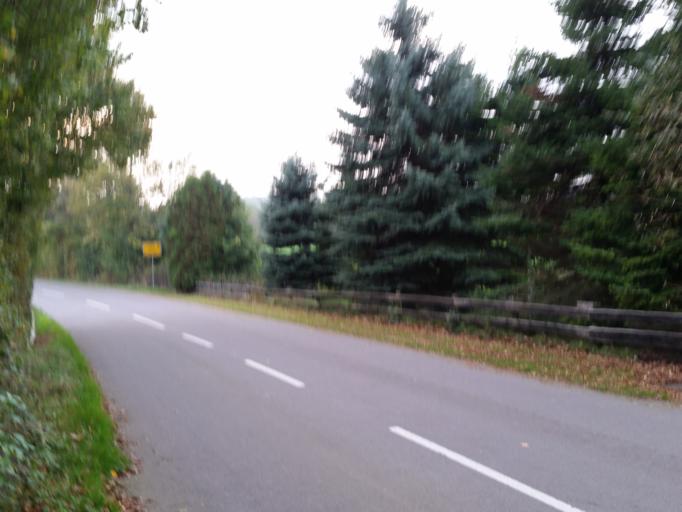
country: DE
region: Schleswig-Holstein
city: Schonwalde am Bungsberg
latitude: 54.1400
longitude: 10.7594
